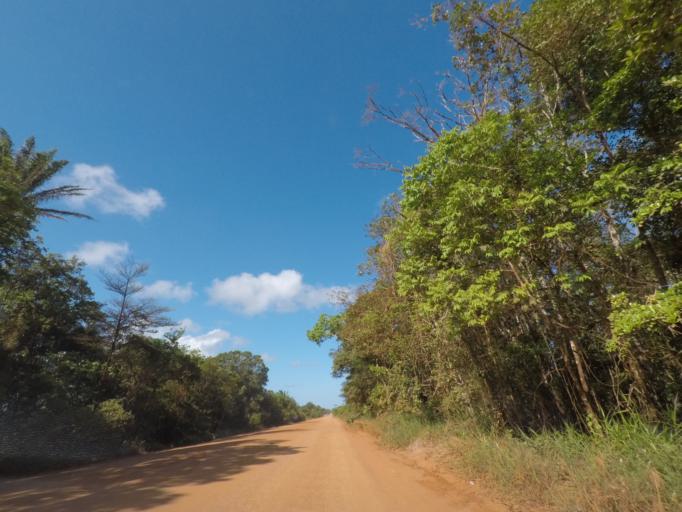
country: BR
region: Bahia
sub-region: Marau
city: Marau
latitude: -14.1548
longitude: -39.0085
